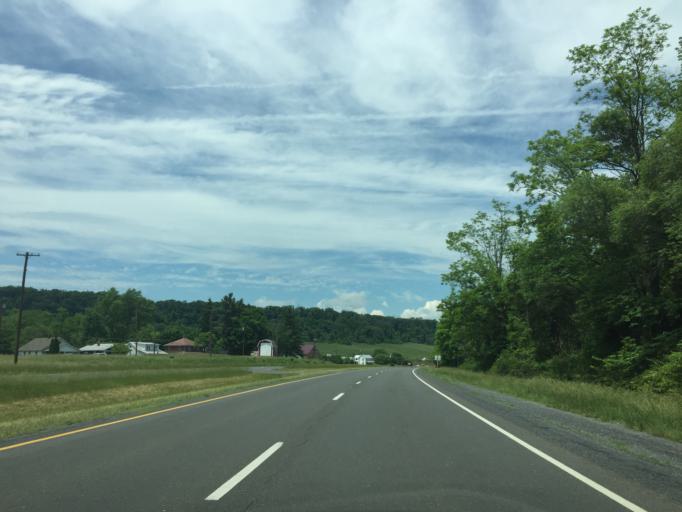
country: US
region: Virginia
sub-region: City of Winchester
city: Winchester
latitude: 39.2244
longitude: -78.1981
